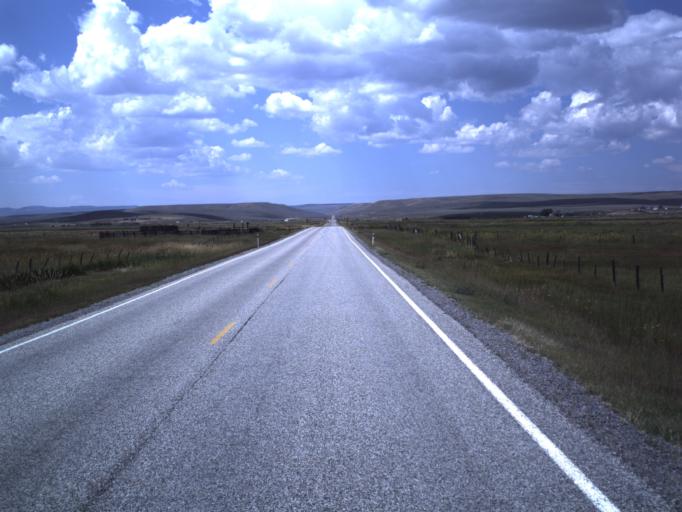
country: US
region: Utah
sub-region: Rich County
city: Randolph
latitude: 41.7746
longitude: -111.1006
